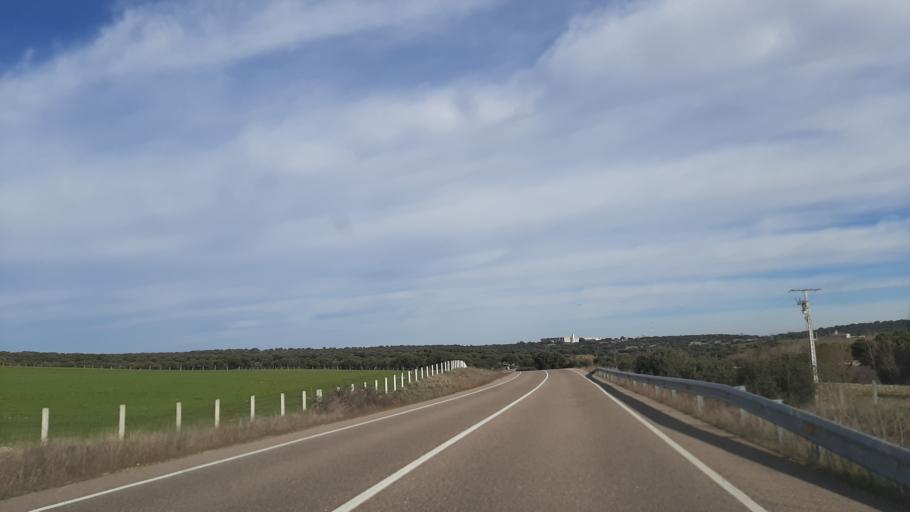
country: ES
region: Castille and Leon
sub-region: Provincia de Salamanca
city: Anover de Tormes
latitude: 41.0890
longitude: -5.9157
